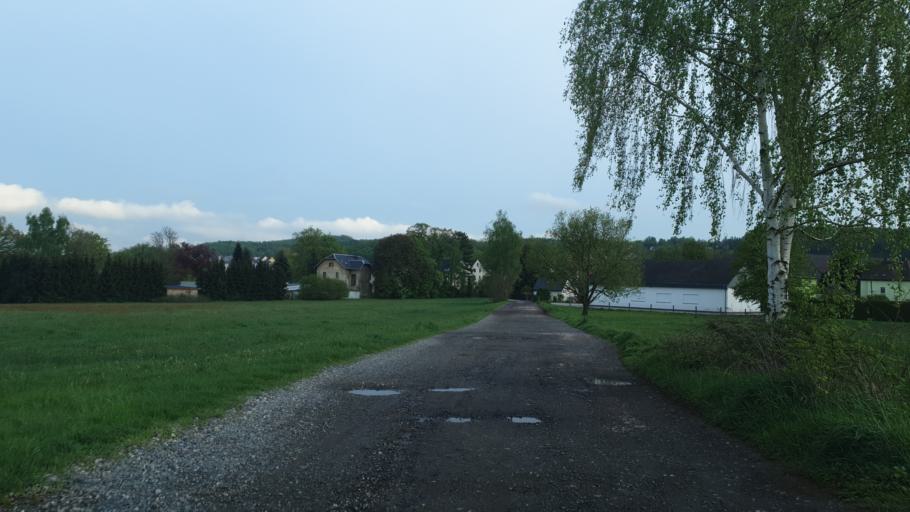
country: DE
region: Saxony
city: Hohndorf
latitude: 50.7443
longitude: 12.6823
